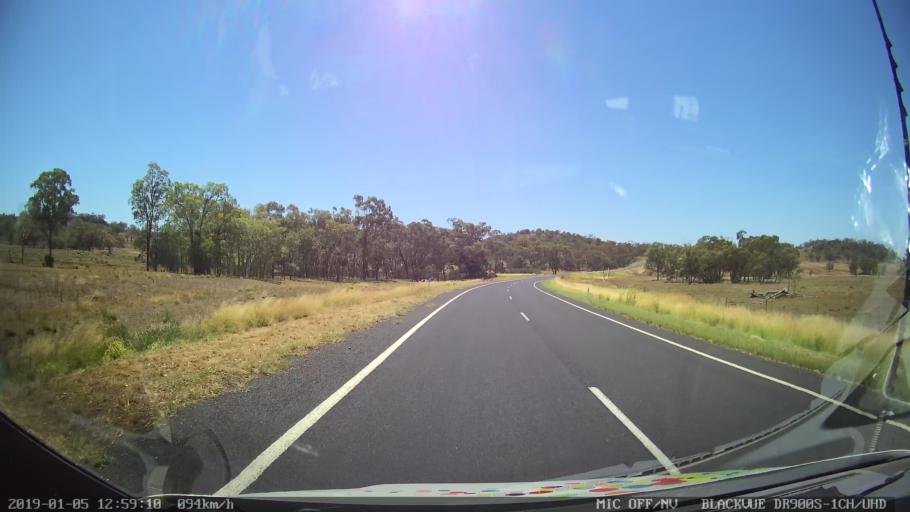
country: AU
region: New South Wales
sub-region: Narrabri
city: Boggabri
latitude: -31.1120
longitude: 149.7615
